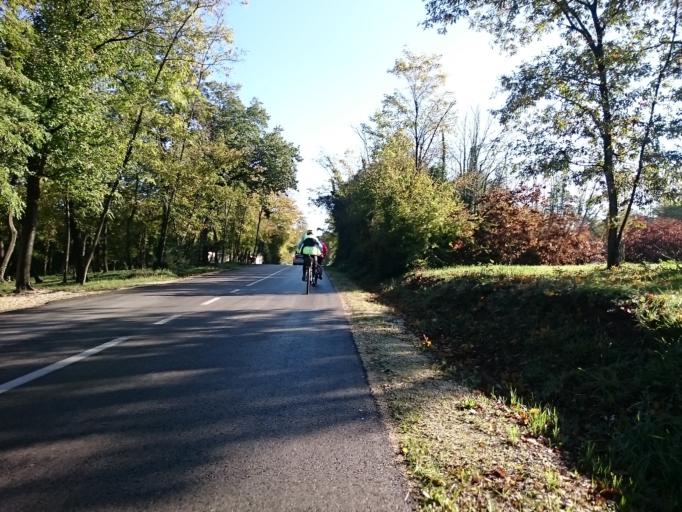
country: HR
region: Istarska
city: Novigrad
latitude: 45.3635
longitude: 13.5950
